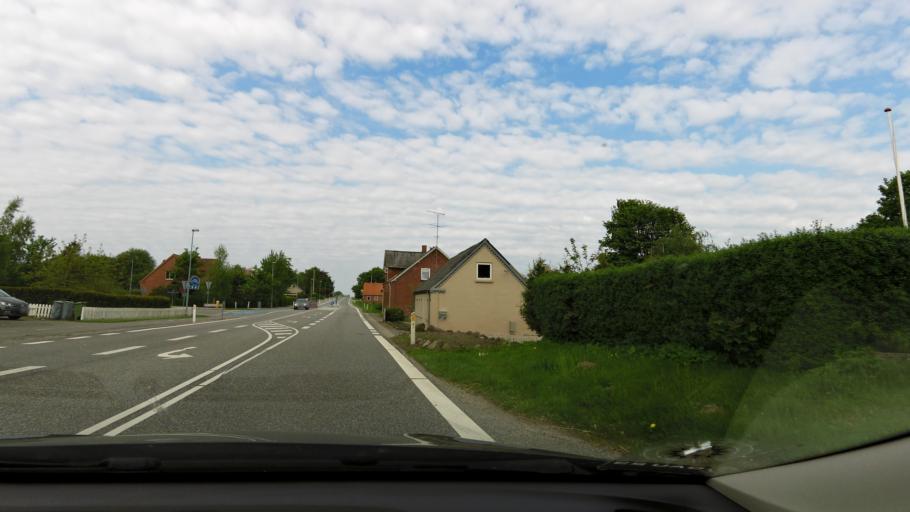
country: DK
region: South Denmark
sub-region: Nyborg Kommune
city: Ullerslev
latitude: 55.2812
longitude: 10.6886
